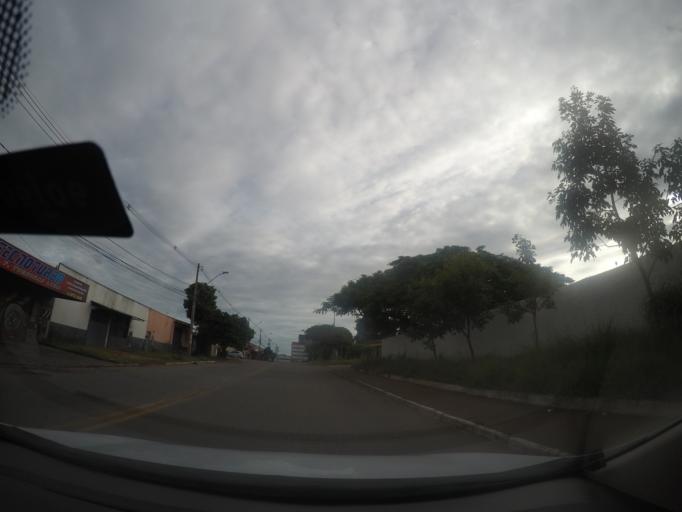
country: BR
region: Goias
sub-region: Goiania
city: Goiania
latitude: -16.6627
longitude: -49.3180
